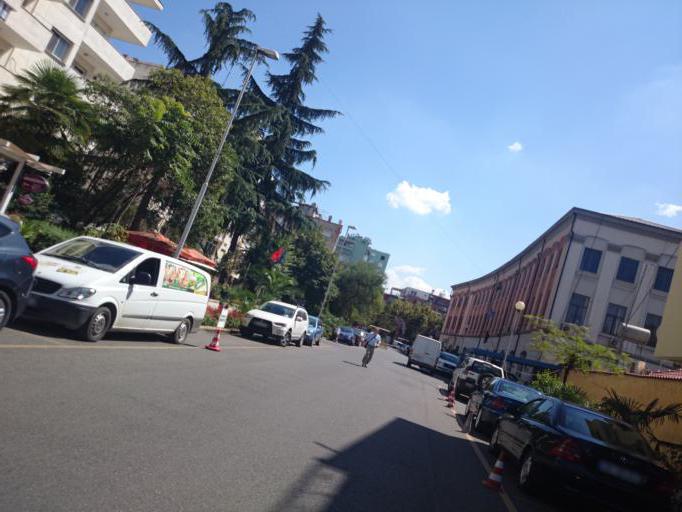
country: AL
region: Tirane
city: Tirana
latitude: 41.3285
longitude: 19.8084
